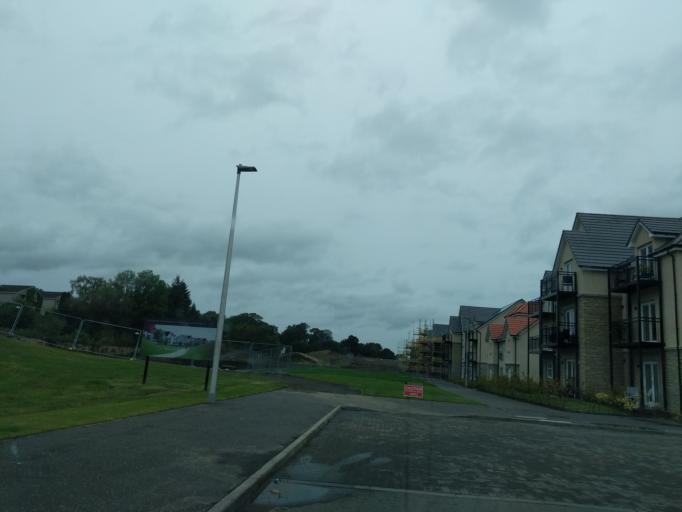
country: GB
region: Scotland
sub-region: Edinburgh
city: Balerno
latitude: 55.8905
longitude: -3.3368
